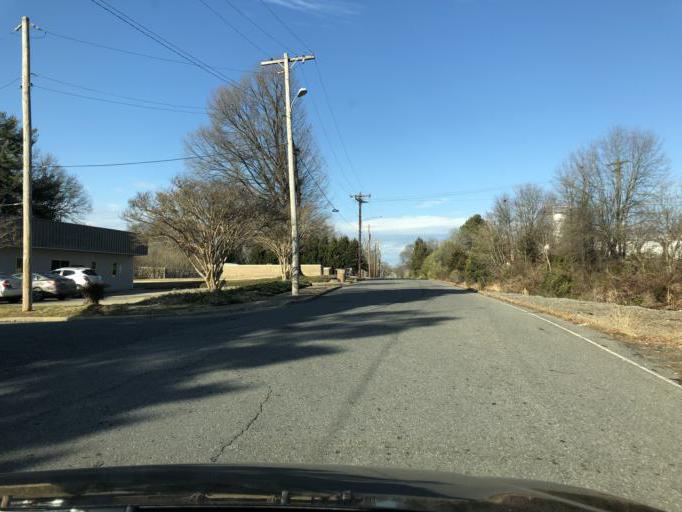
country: US
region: North Carolina
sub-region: Cleveland County
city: Shelby
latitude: 35.2805
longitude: -81.5427
